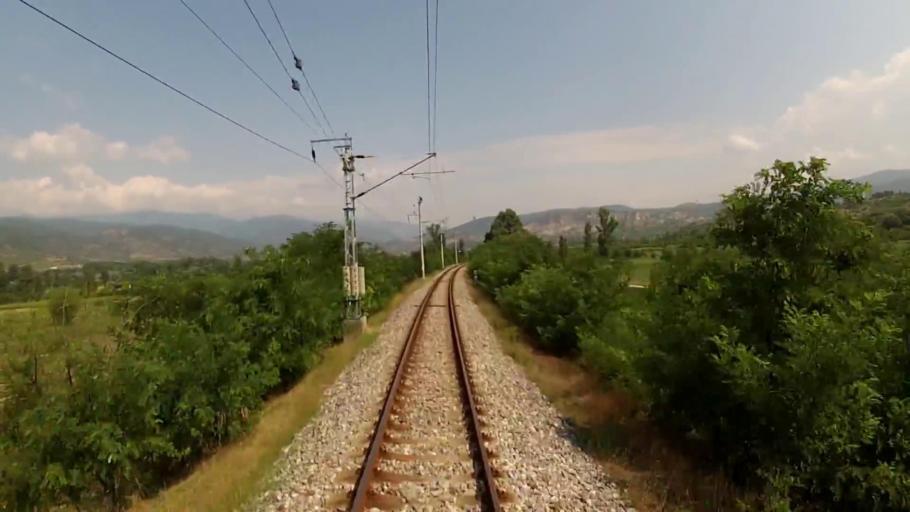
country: BG
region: Blagoevgrad
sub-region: Obshtina Strumyani
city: Strumyani
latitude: 41.6695
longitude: 23.1831
